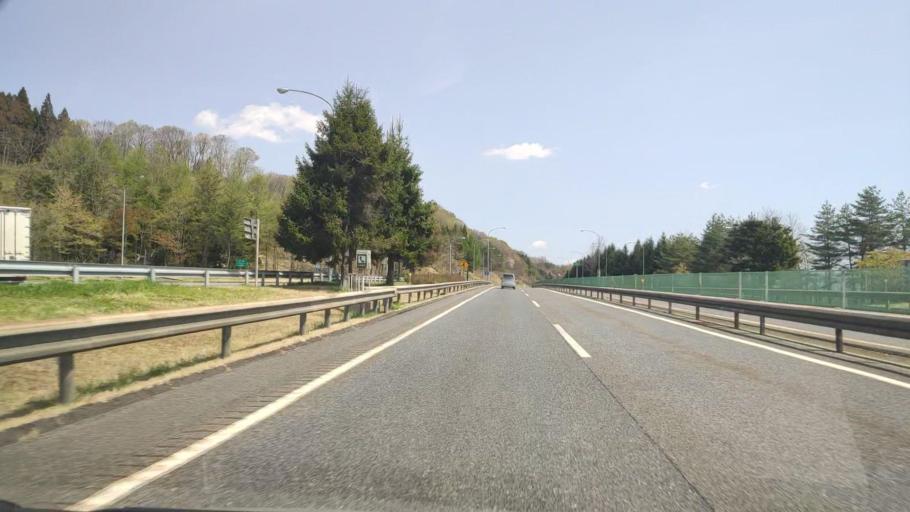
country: JP
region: Iwate
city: Ichinohe
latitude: 40.2108
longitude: 141.2188
